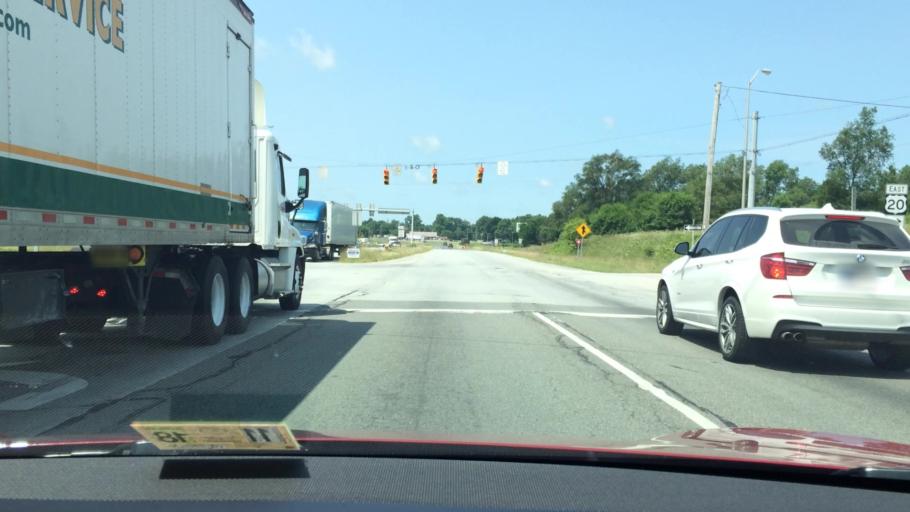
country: US
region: Indiana
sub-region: LaPorte County
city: Hudson Lake
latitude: 41.6730
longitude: -86.5886
